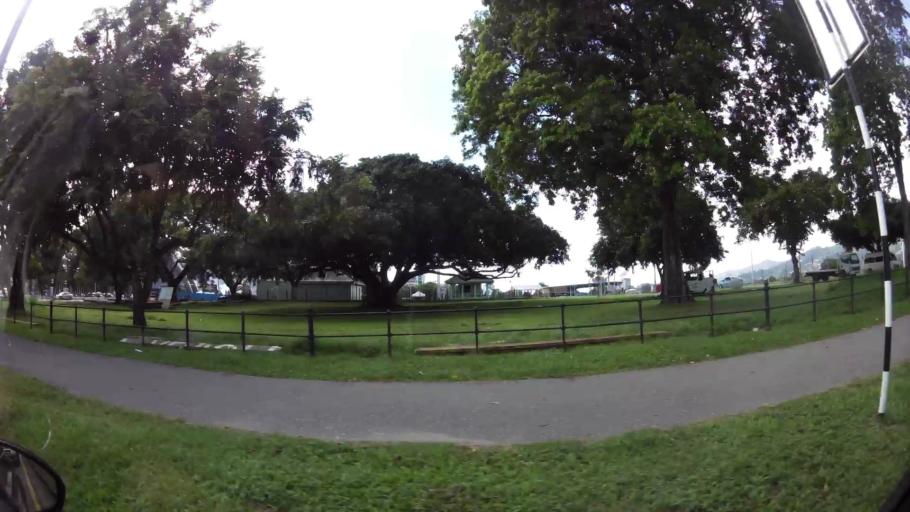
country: TT
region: City of Port of Spain
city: Port-of-Spain
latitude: 10.6651
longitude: -61.5093
